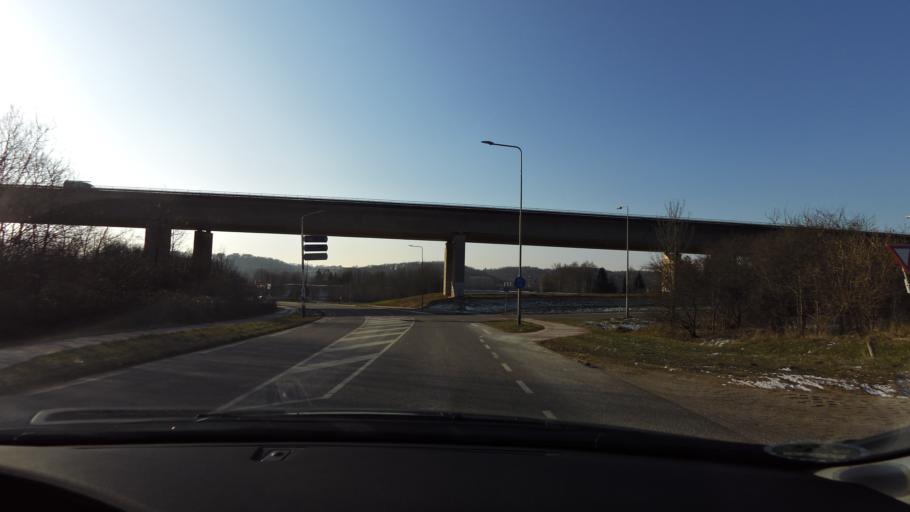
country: NL
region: Limburg
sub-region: Valkenburg aan de Geul
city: Broekhem
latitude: 50.8752
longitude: 5.8132
